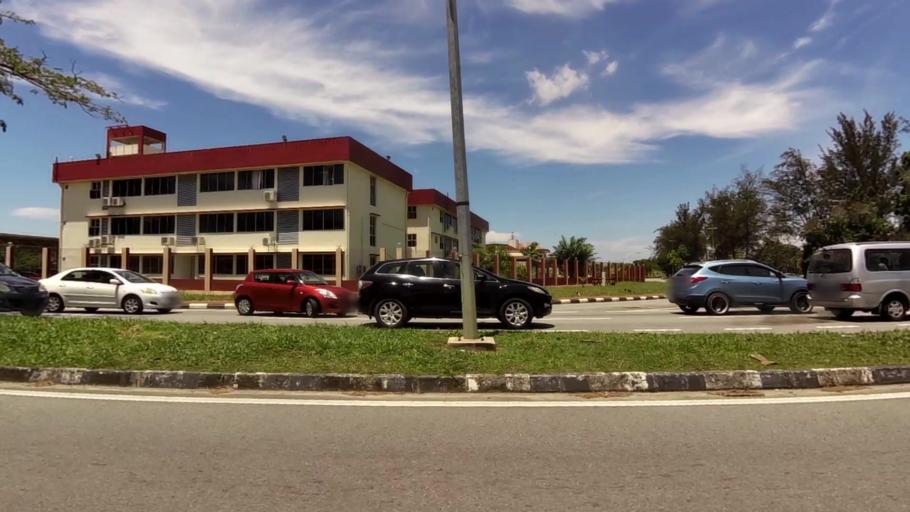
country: BN
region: Brunei and Muara
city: Bandar Seri Begawan
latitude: 4.9265
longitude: 114.9332
